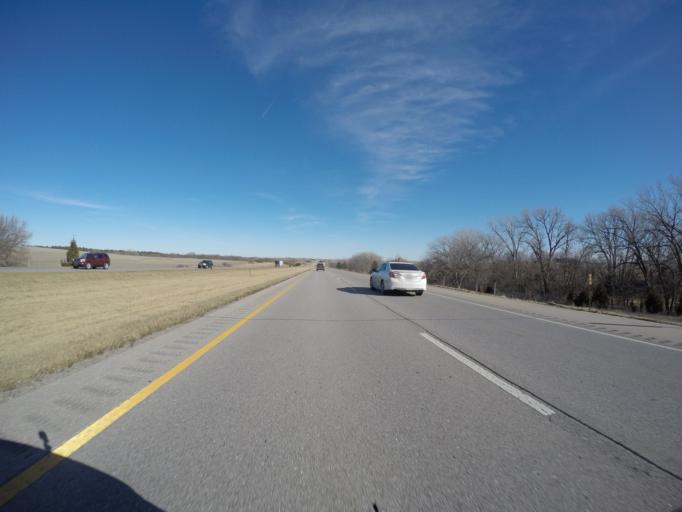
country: US
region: Nebraska
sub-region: Seward County
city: Milford
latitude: 40.8212
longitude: -96.9745
